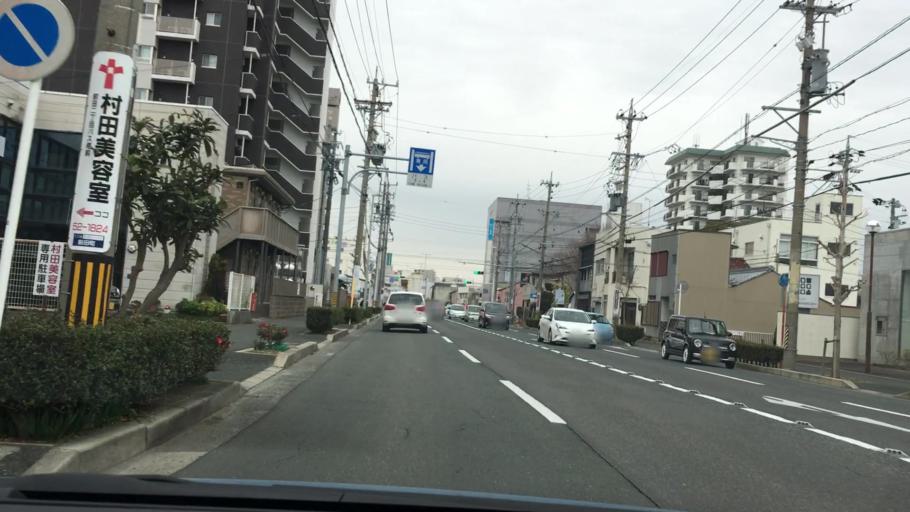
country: JP
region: Aichi
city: Toyohashi
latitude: 34.7609
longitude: 137.3976
